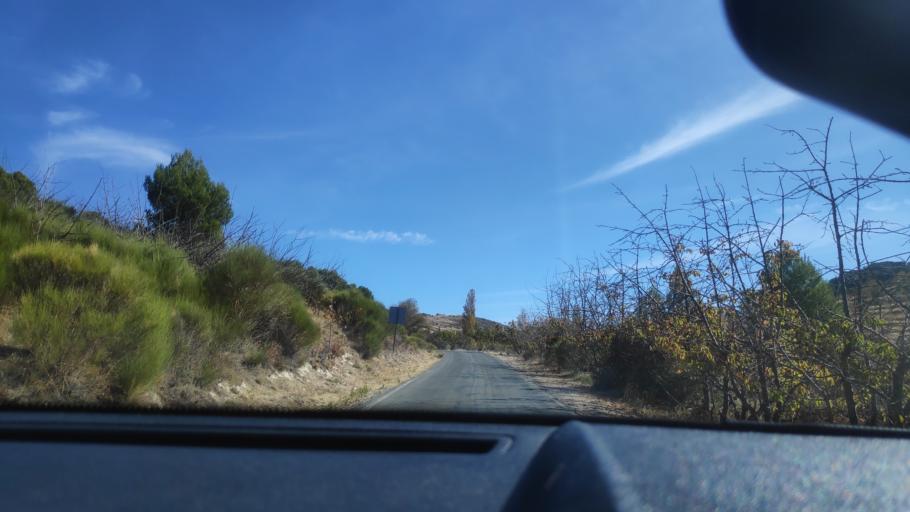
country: ES
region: Andalusia
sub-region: Provincia de Jaen
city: Torres
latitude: 37.7864
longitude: -3.4896
